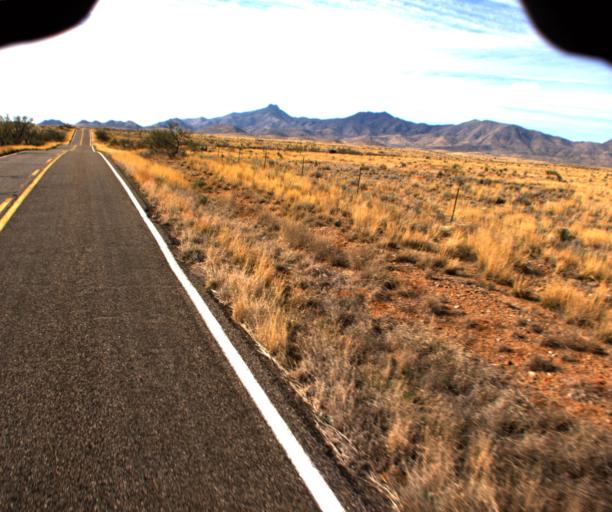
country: US
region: Arizona
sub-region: Cochise County
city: Willcox
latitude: 32.0984
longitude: -109.5395
